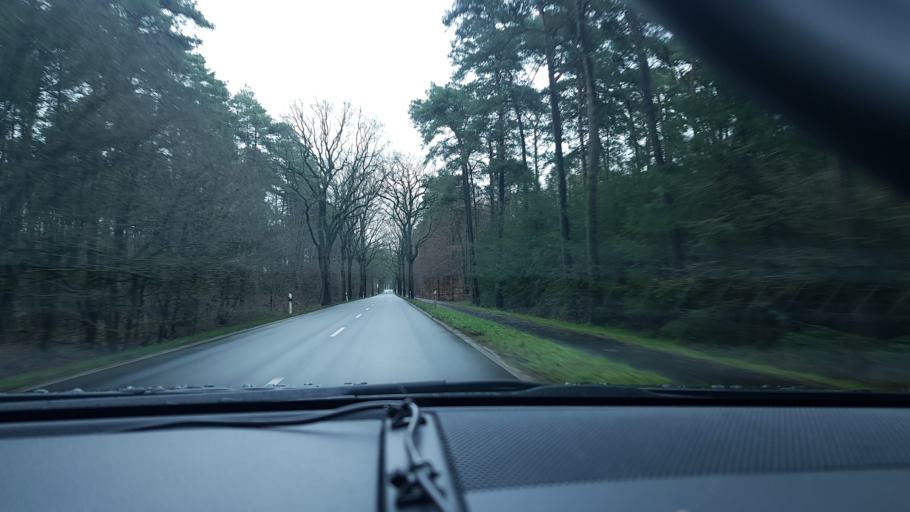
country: DE
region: North Rhine-Westphalia
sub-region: Regierungsbezirk Dusseldorf
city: Bruggen
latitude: 51.2398
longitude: 6.1411
